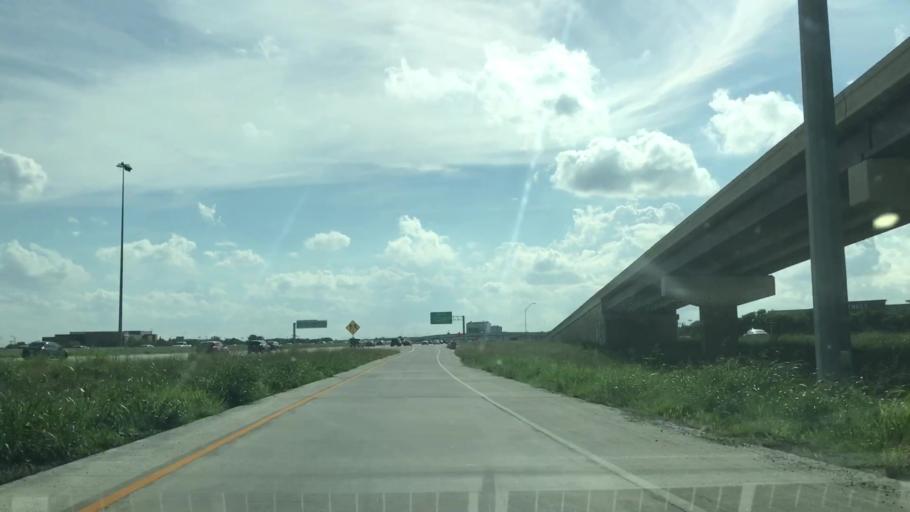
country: US
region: Texas
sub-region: Dallas County
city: Coppell
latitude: 32.9707
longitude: -97.0313
